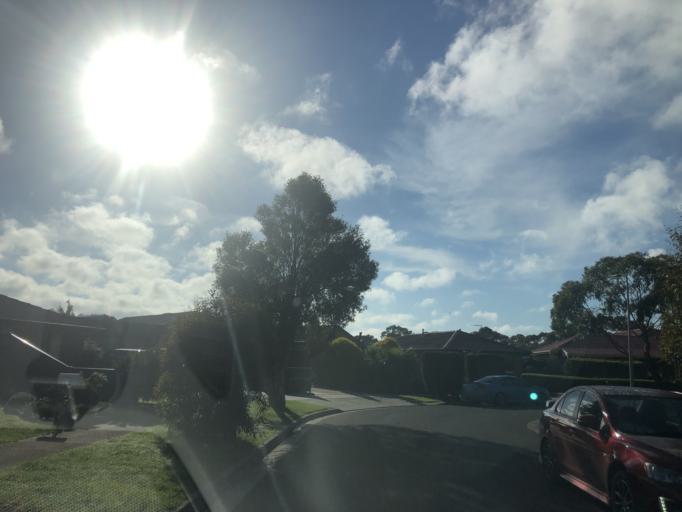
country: AU
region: Victoria
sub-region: Casey
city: Eumemmerring
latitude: -37.9969
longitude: 145.2610
